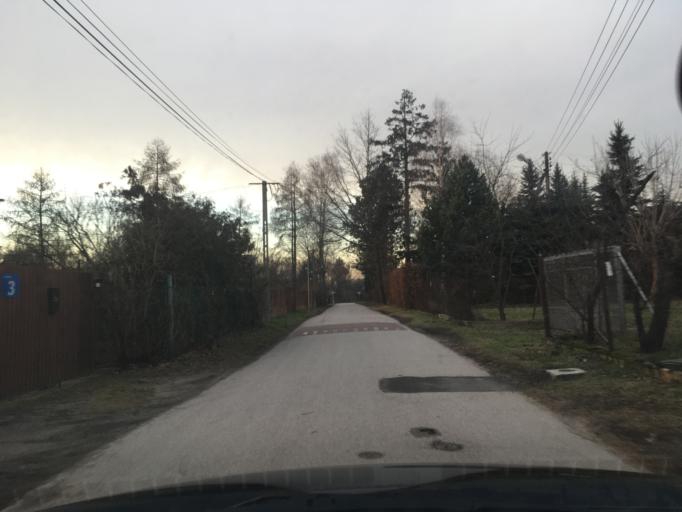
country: PL
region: Masovian Voivodeship
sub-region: Powiat piaseczynski
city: Lesznowola
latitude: 52.0384
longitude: 20.9518
